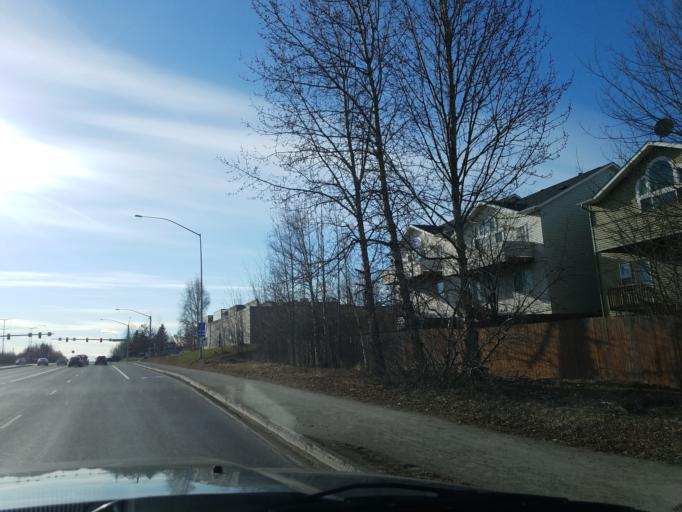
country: US
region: Alaska
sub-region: Anchorage Municipality
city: Anchorage
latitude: 61.1808
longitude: -149.7756
